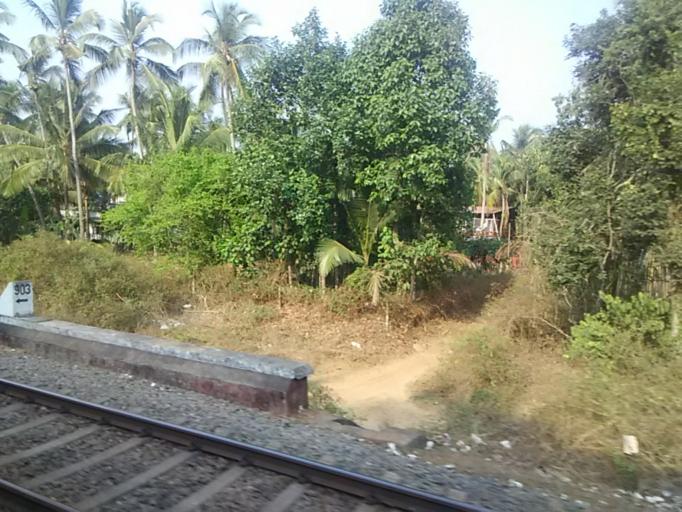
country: IN
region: Kerala
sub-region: Malappuram
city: Pariyapuram
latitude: 11.0114
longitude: 75.8726
